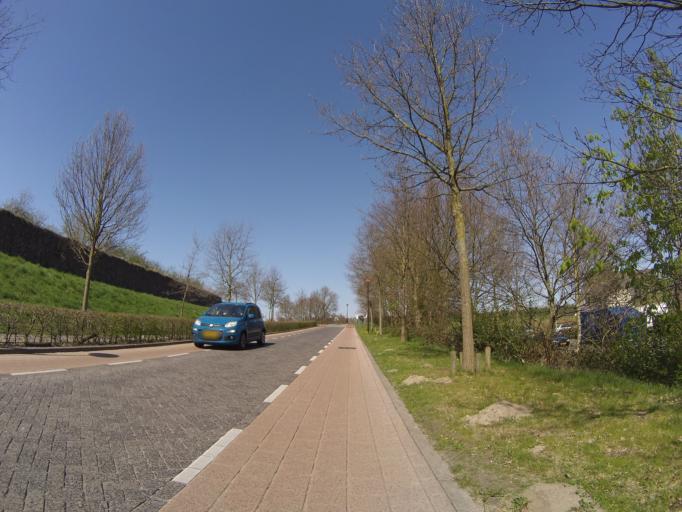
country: NL
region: Utrecht
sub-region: Gemeente Amersfoort
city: Hoogland
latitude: 52.2020
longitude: 5.3884
